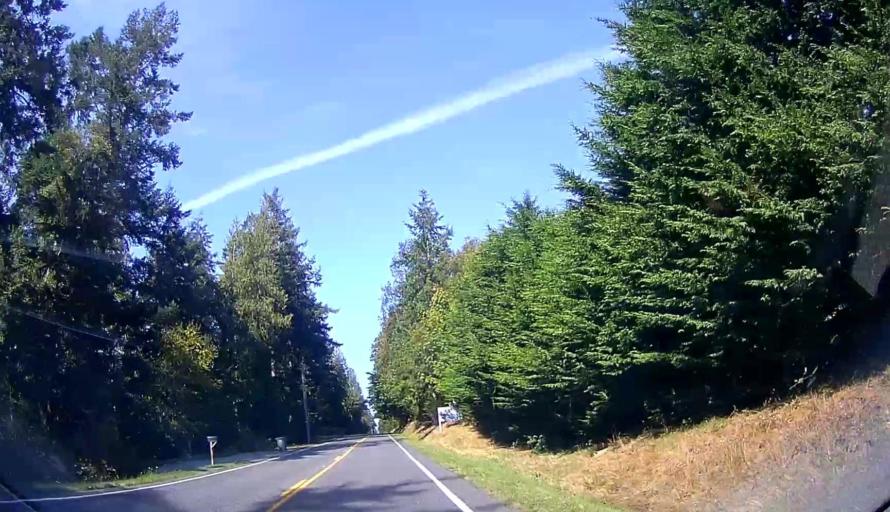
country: US
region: Washington
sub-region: Island County
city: Camano
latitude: 48.2271
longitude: -122.5211
